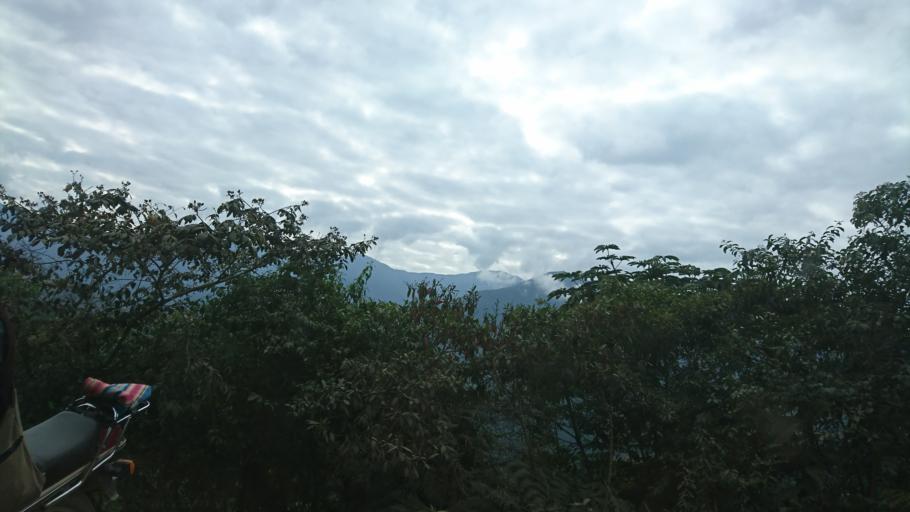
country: BO
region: La Paz
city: Coroico
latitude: -16.2325
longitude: -67.6798
